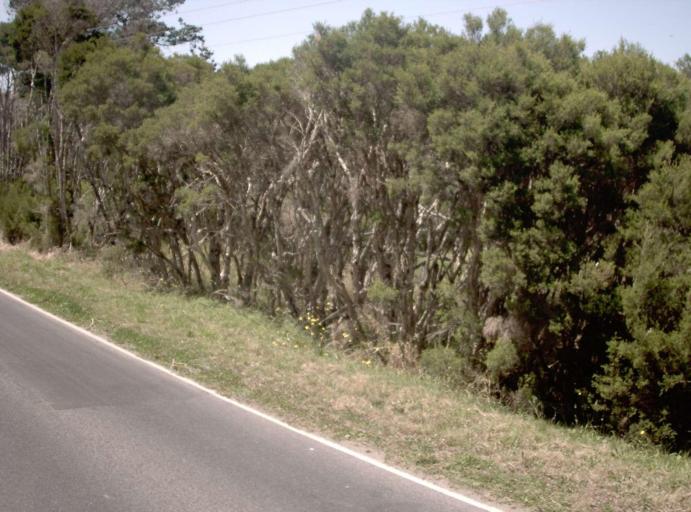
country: AU
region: Victoria
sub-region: Bass Coast
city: North Wonthaggi
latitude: -38.6299
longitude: 145.8355
